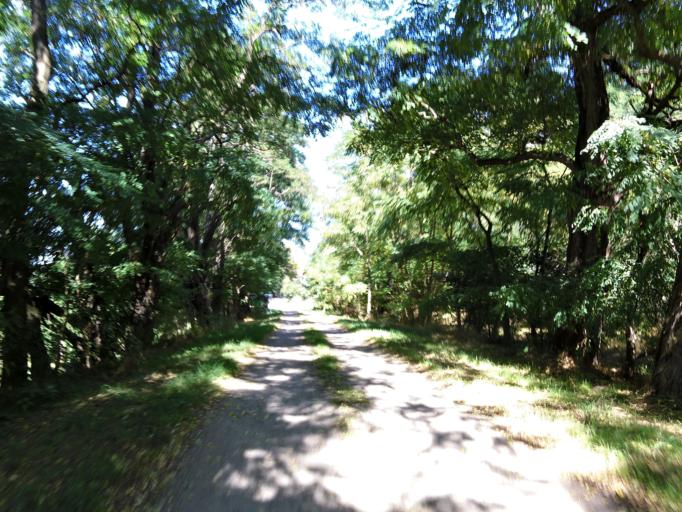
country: DE
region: Saxony
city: Strehla
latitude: 51.3932
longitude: 13.2468
